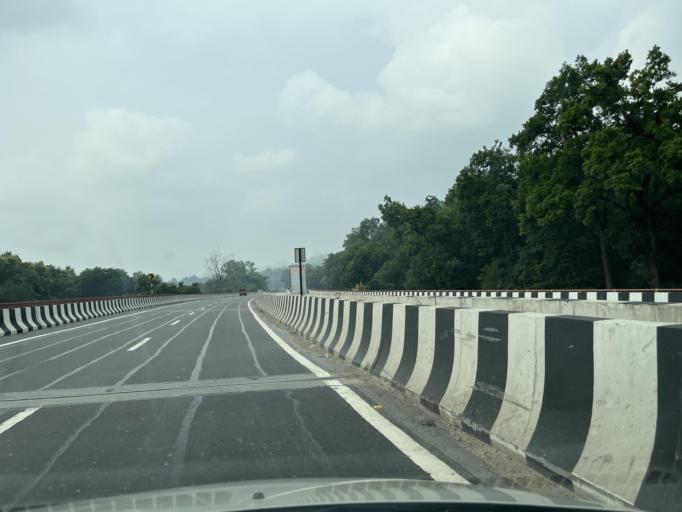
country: IN
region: Uttarakhand
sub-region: Dehradun
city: Raiwala
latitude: 30.0132
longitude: 78.1951
